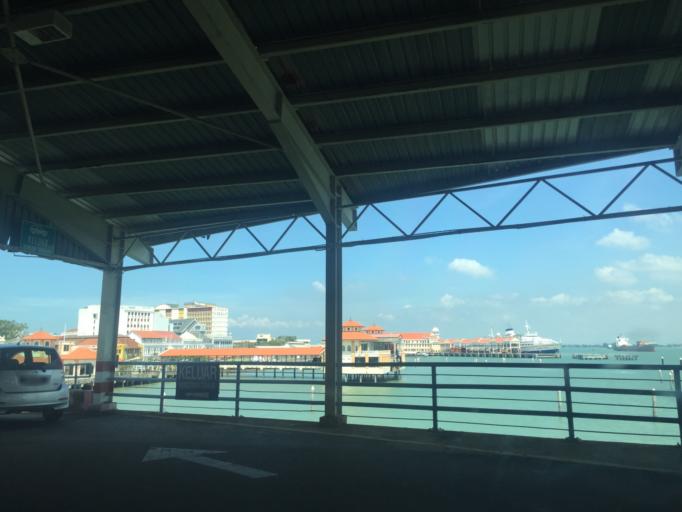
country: MY
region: Penang
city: George Town
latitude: 5.4133
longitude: 100.3437
